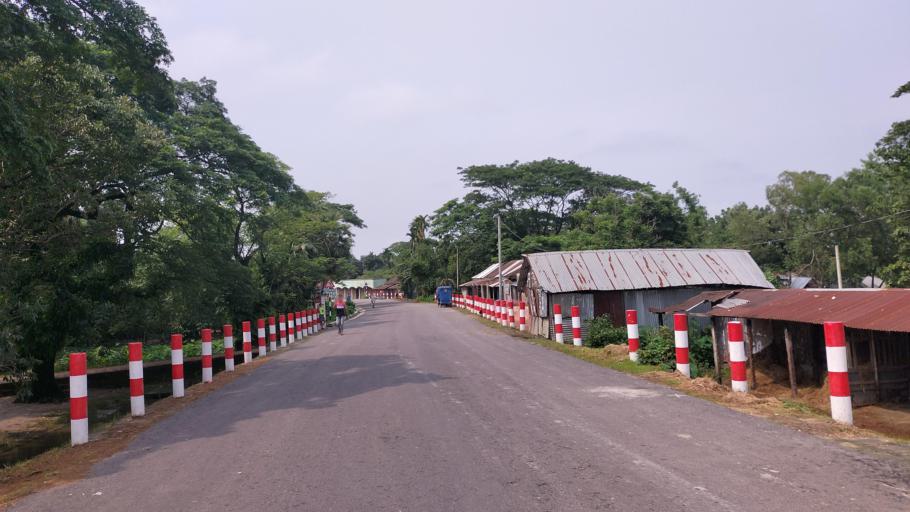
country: BD
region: Dhaka
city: Netrakona
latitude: 24.9563
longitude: 90.8347
